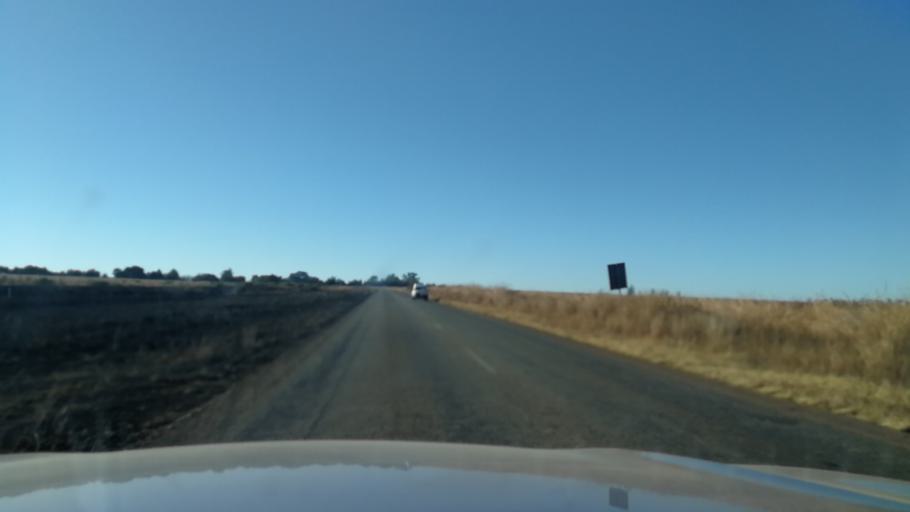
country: ZA
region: North-West
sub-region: Bojanala Platinum District Municipality
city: Rustenburg
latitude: -25.9481
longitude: 27.1760
